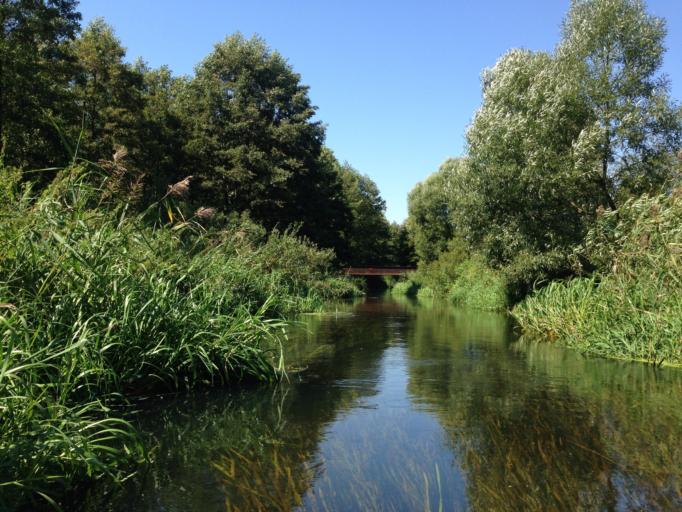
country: PL
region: Kujawsko-Pomorskie
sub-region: Powiat brodnicki
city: Bartniczka
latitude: 53.2817
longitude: 19.5745
